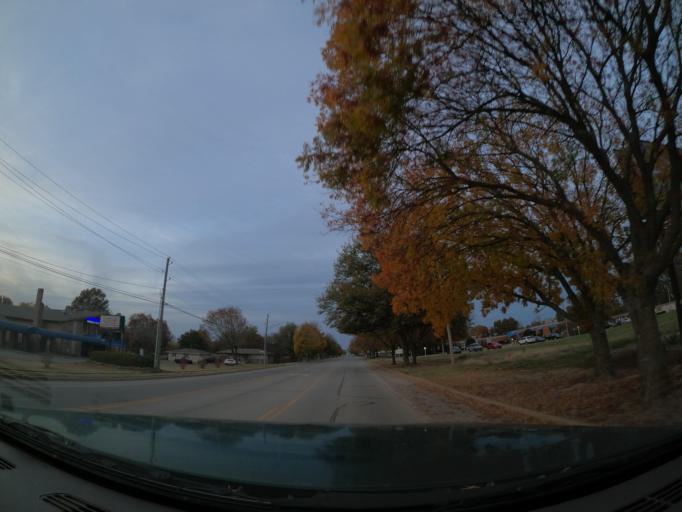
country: US
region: Oklahoma
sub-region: Tulsa County
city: Broken Arrow
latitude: 36.0336
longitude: -95.7908
